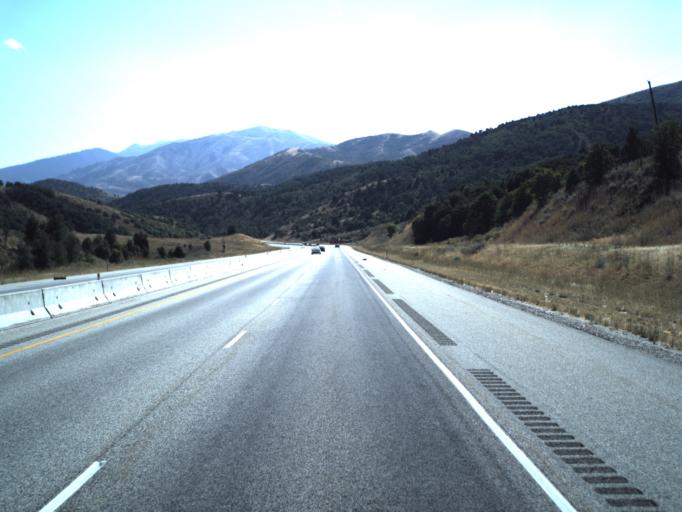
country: US
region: Utah
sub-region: Box Elder County
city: Brigham City
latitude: 41.5441
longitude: -111.9563
